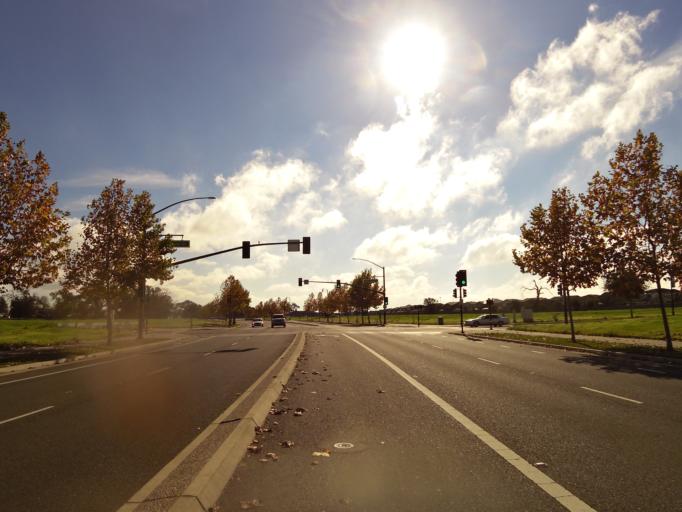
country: US
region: California
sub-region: Sacramento County
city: Elk Grove
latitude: 38.4070
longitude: -121.3957
